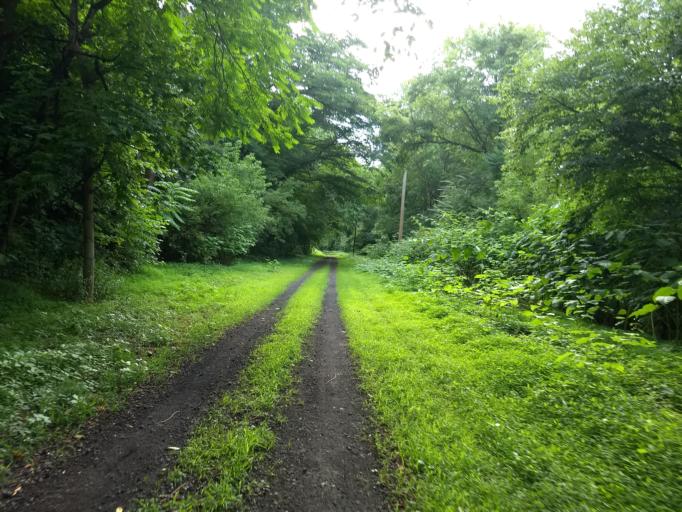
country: US
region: Pennsylvania
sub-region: Armstrong County
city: Freeport
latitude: 40.6694
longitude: -79.6830
